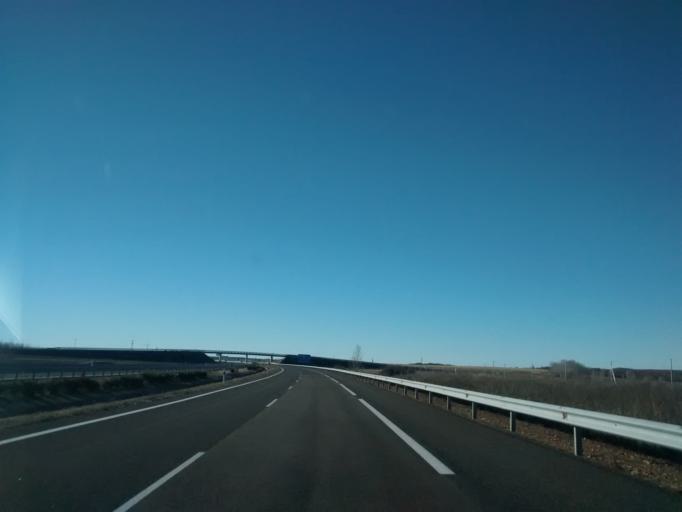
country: ES
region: Castille and Leon
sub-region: Provincia de Palencia
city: San Cristobal de Boedo
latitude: 42.5512
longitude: -4.3729
